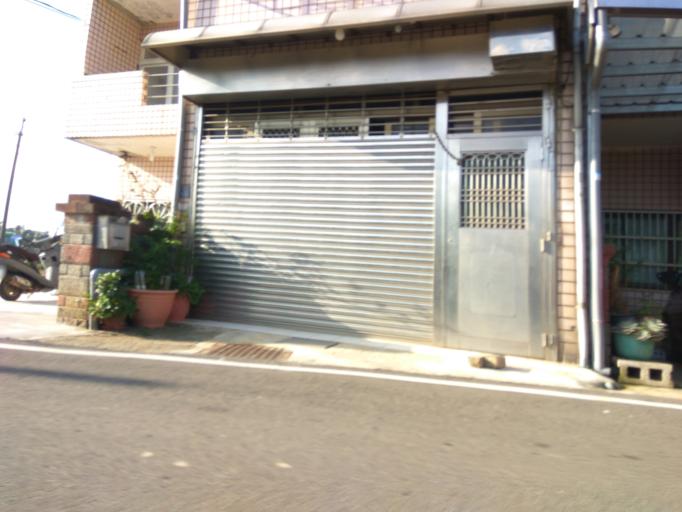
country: TW
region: Taiwan
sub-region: Hsinchu
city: Zhubei
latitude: 24.9822
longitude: 121.0543
